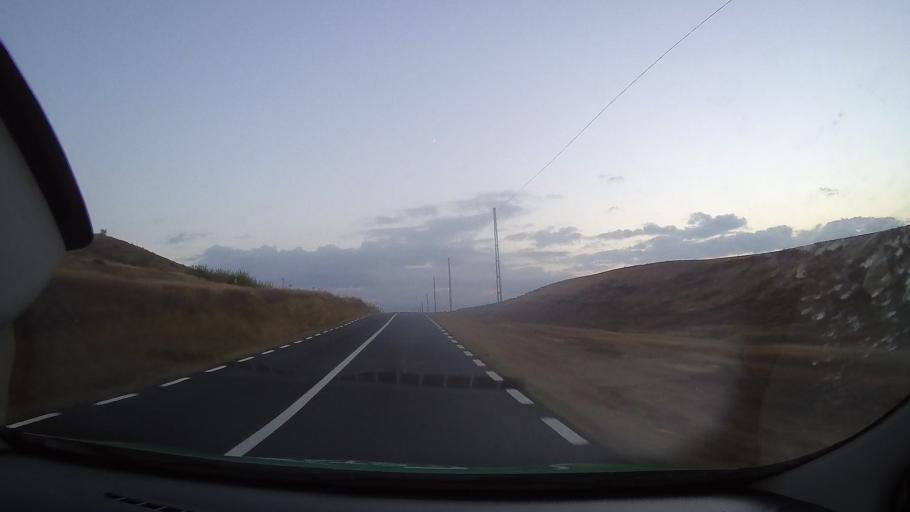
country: RO
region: Constanta
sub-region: Comuna Oltina
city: Oltina
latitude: 44.1461
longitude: 27.6666
